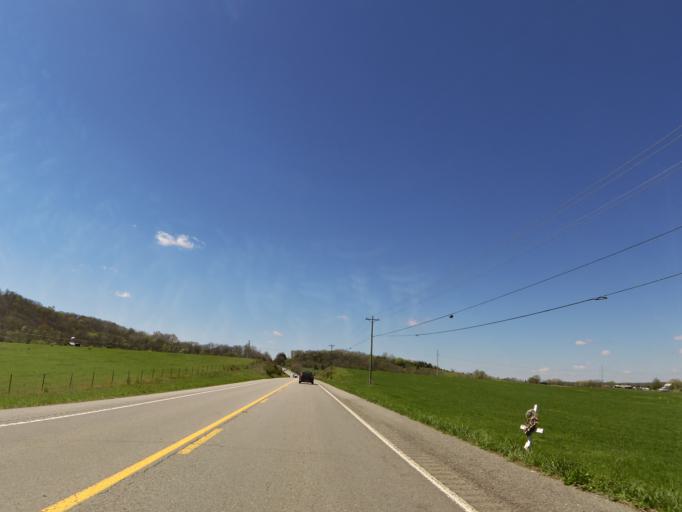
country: US
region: Tennessee
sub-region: White County
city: Sparta
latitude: 35.9474
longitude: -85.5280
